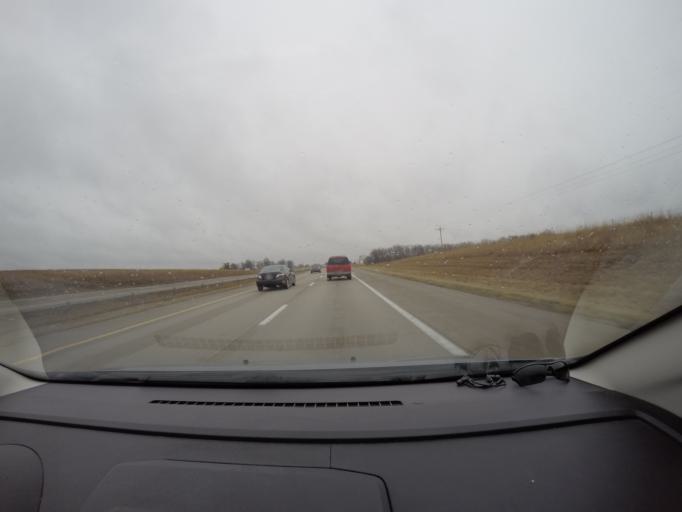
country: US
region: Missouri
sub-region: Callaway County
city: Fulton
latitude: 38.9236
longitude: -91.7684
